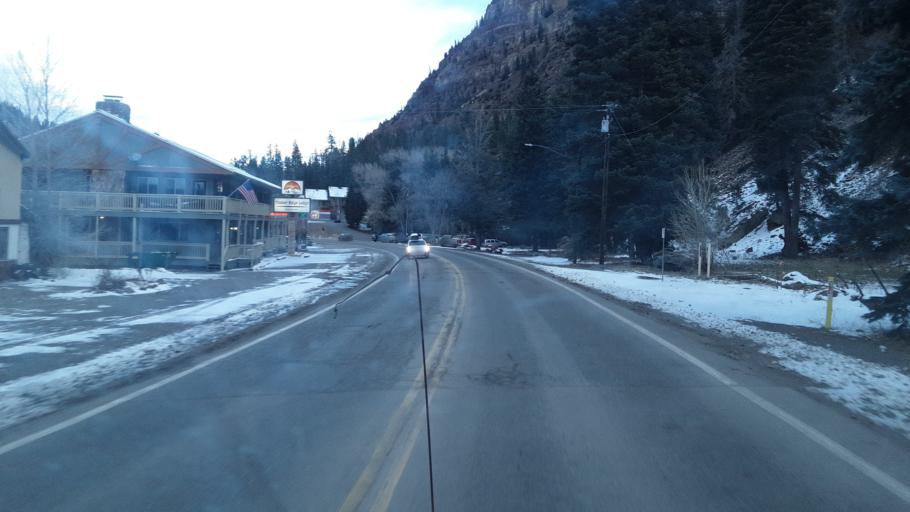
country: US
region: Colorado
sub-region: Ouray County
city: Ouray
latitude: 38.0334
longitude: -107.6745
